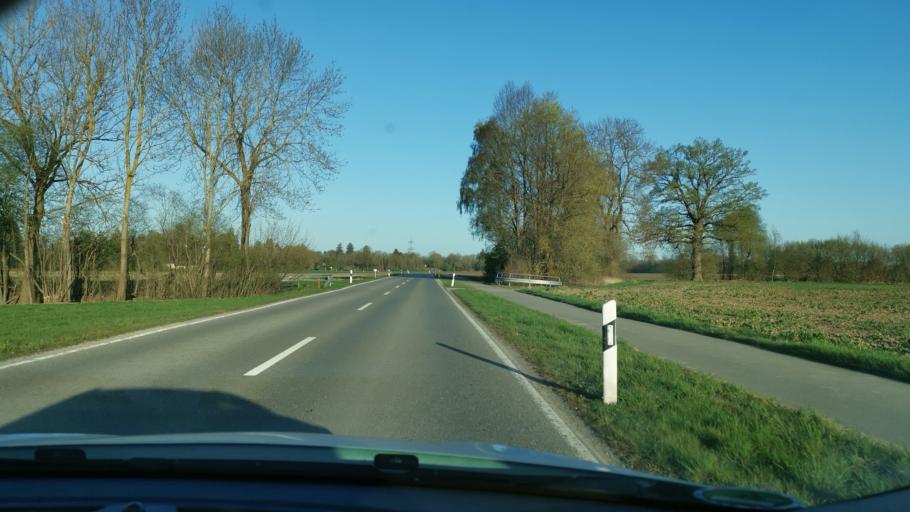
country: DE
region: Bavaria
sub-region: Swabia
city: Langweid
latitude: 48.4886
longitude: 10.8908
